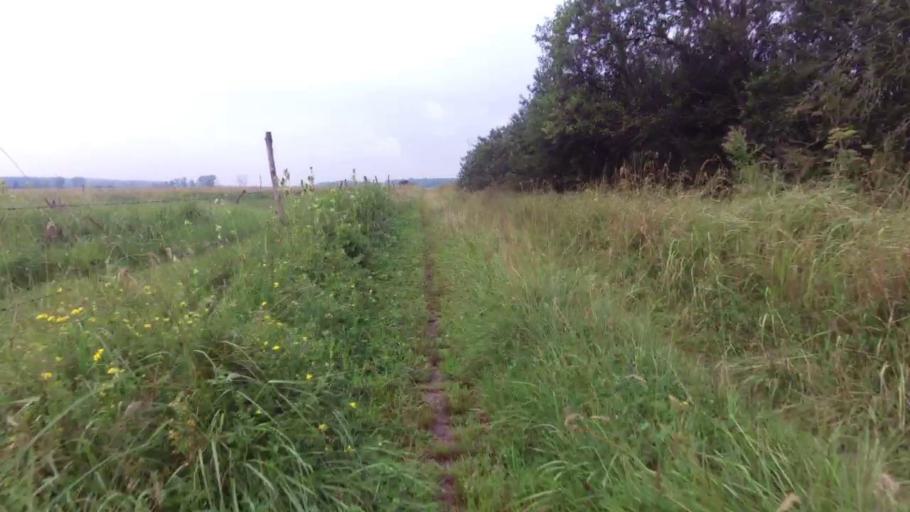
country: PL
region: West Pomeranian Voivodeship
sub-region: Powiat stargardzki
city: Suchan
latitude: 53.2509
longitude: 15.3993
